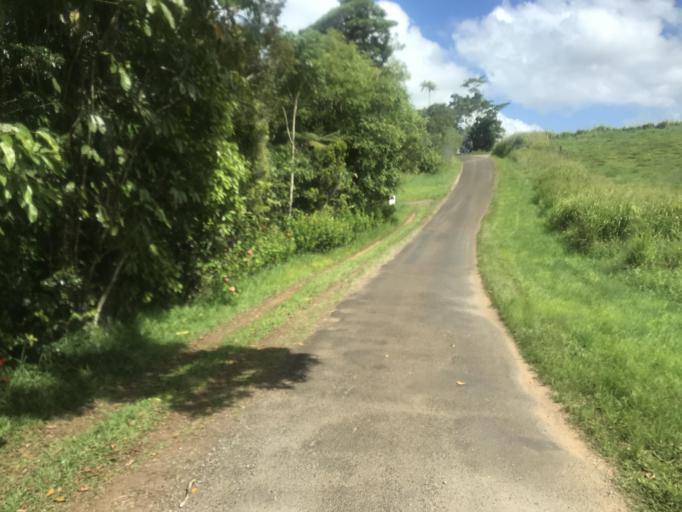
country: AU
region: Queensland
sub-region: Tablelands
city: Ravenshoe
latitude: -17.5446
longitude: 145.6935
